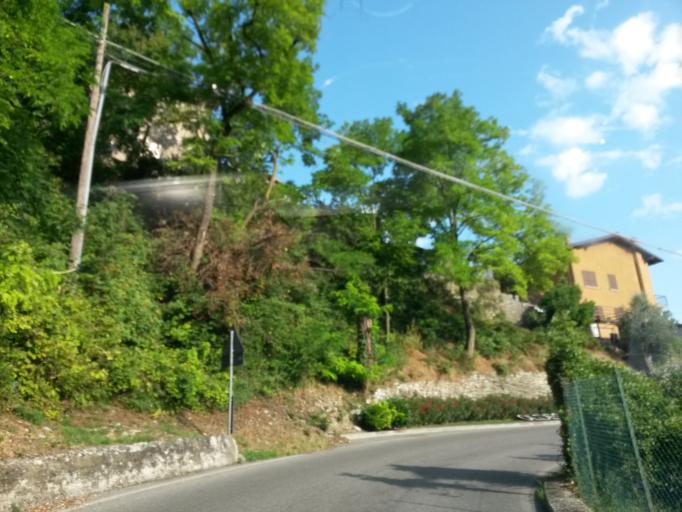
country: IT
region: Lombardy
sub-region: Provincia di Brescia
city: Gardola
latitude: 45.7350
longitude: 10.7182
